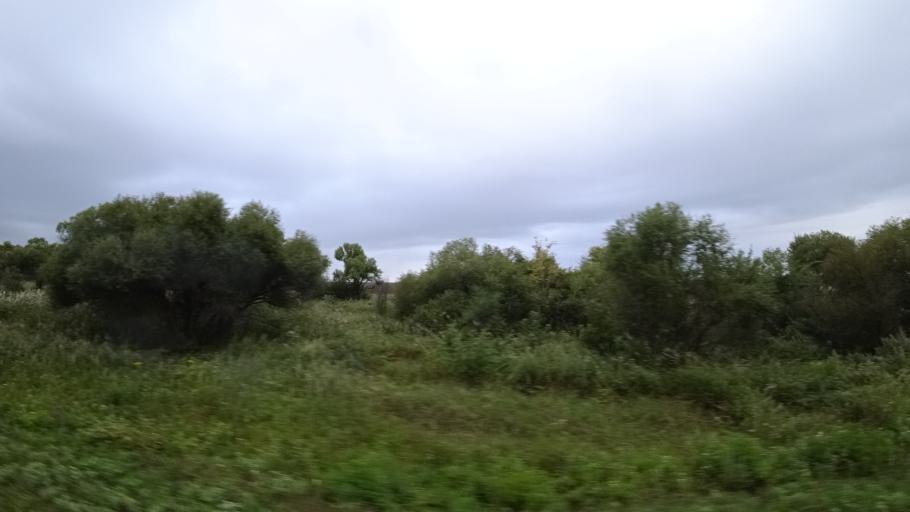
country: RU
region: Primorskiy
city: Chernigovka
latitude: 44.3637
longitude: 132.5468
